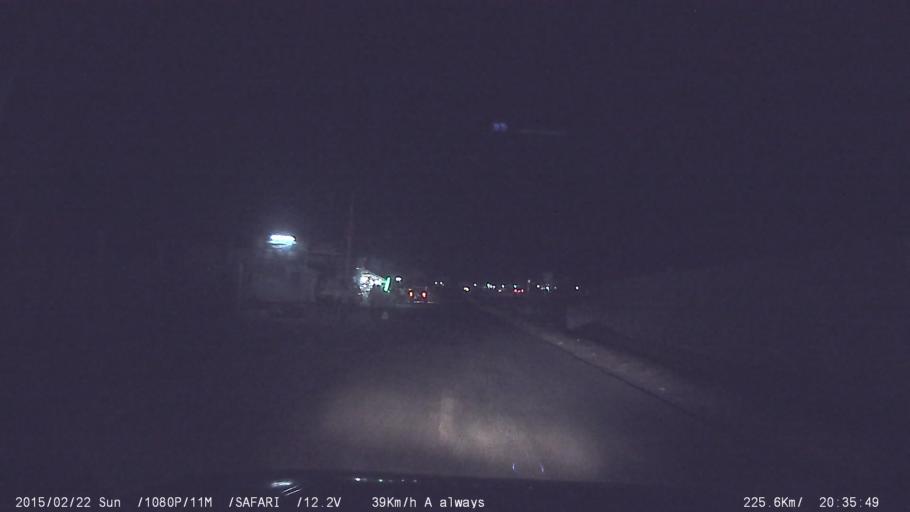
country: IN
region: Tamil Nadu
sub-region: Dindigul
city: Dindigul
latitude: 10.3750
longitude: 77.9538
